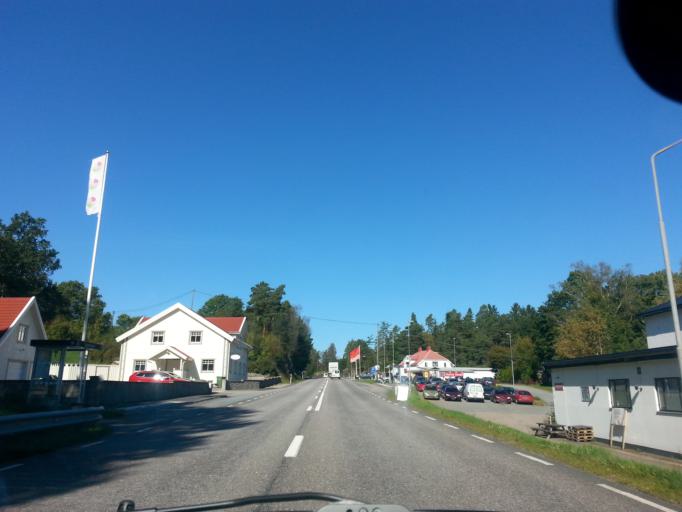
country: SE
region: Vaestra Goetaland
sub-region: Harryda Kommun
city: Ravlanda
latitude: 57.5480
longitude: 12.5326
